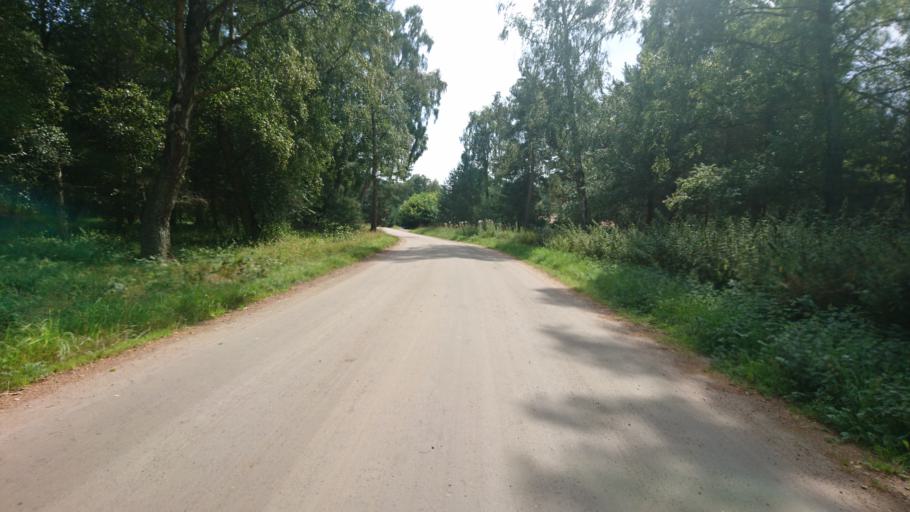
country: SE
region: Skane
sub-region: Vellinge Kommun
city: Ljunghusen
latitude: 55.3981
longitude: 12.9121
